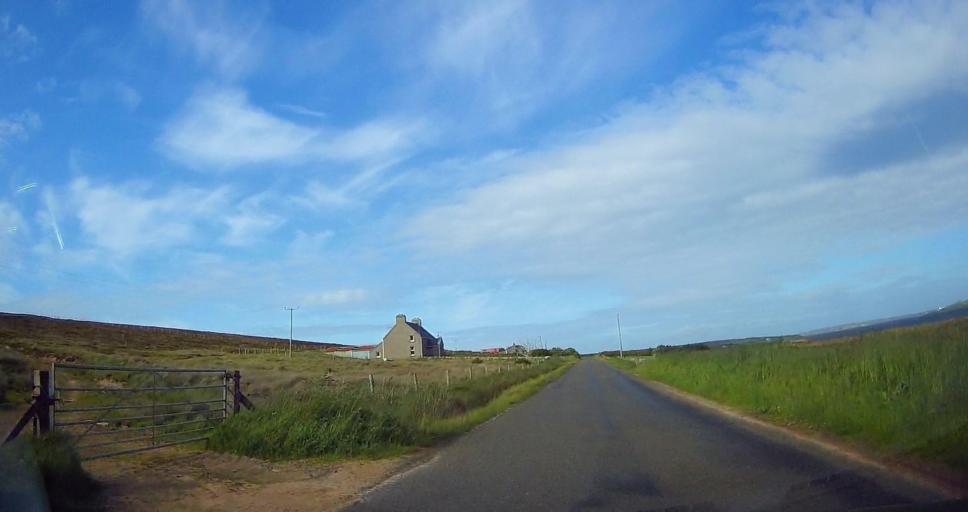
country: GB
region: Scotland
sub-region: Orkney Islands
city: Stromness
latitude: 58.7914
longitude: -3.2583
